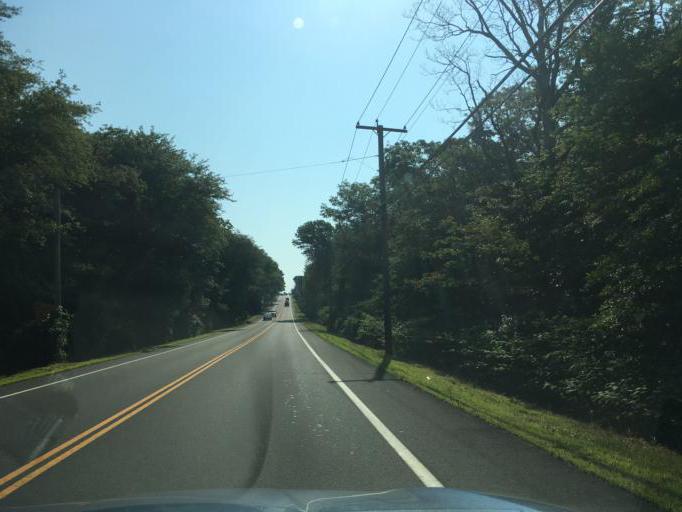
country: US
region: Rhode Island
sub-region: Washington County
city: North Kingstown
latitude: 41.4937
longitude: -71.4657
